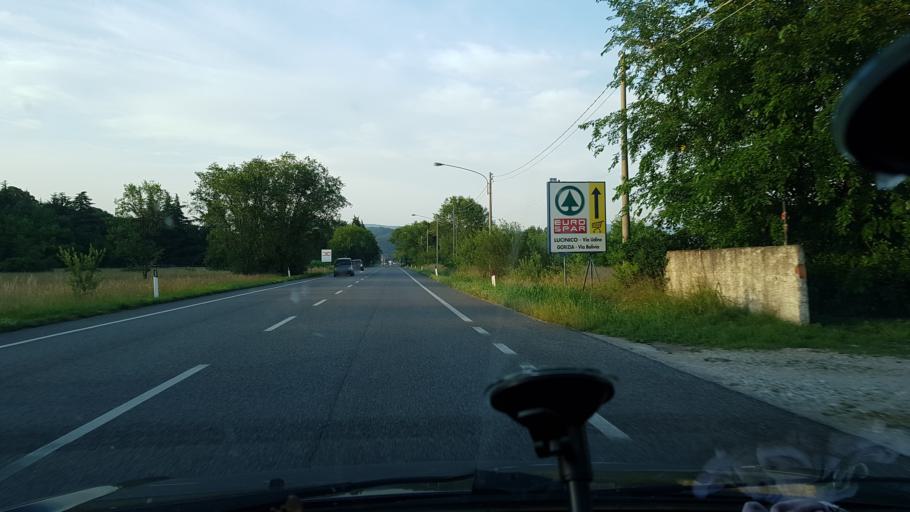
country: IT
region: Friuli Venezia Giulia
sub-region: Provincia di Gorizia
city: Savogna d'Isonzo
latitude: 45.9173
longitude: 13.5626
